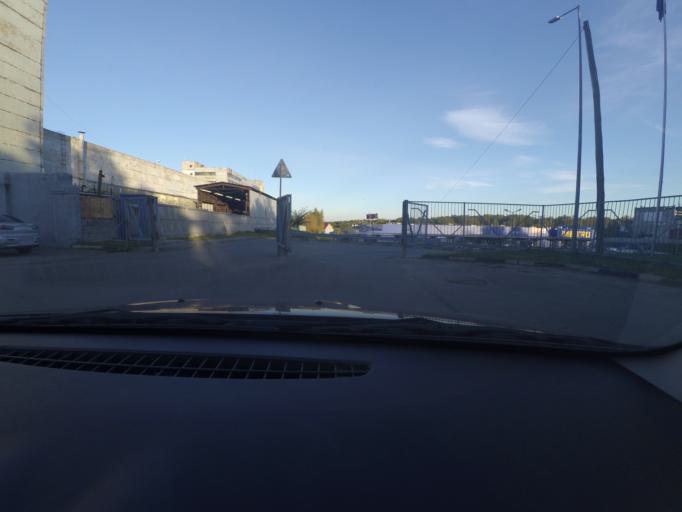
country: RU
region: Nizjnij Novgorod
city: Nizhniy Novgorod
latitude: 56.2878
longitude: 43.9950
